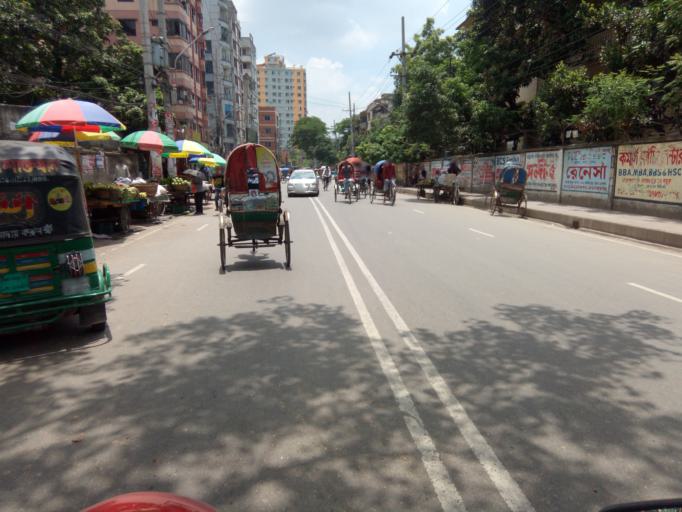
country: BD
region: Dhaka
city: Azimpur
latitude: 23.7264
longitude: 90.3853
